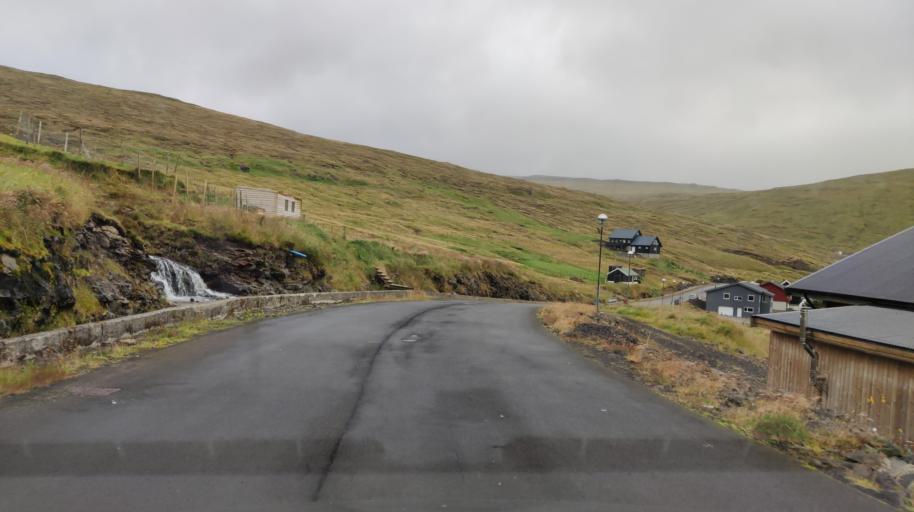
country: FO
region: Streymoy
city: Vestmanna
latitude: 62.1549
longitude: -7.1851
